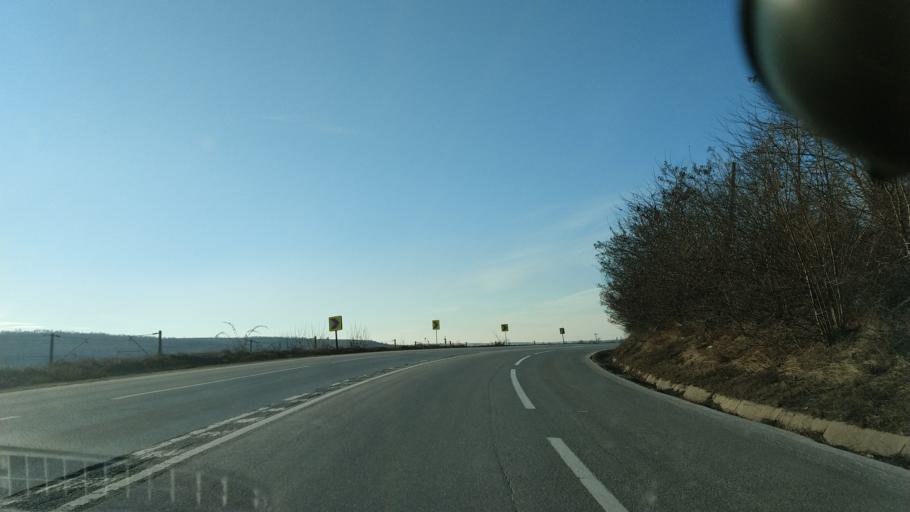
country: RO
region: Iasi
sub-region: Comuna Baltati
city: Baltati
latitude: 47.2224
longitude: 27.1759
